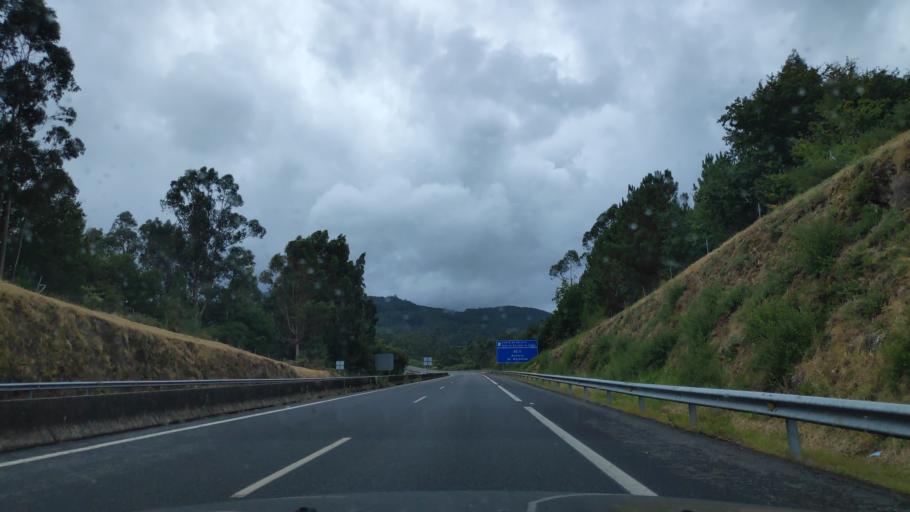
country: ES
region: Galicia
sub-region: Provincia da Coruna
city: Padron
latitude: 42.7285
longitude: -8.6843
